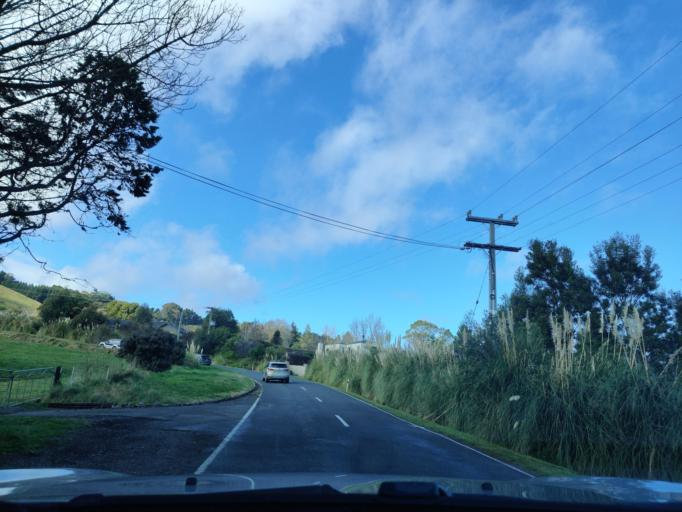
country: NZ
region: Hawke's Bay
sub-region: Hastings District
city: Hastings
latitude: -39.6888
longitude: 176.8991
